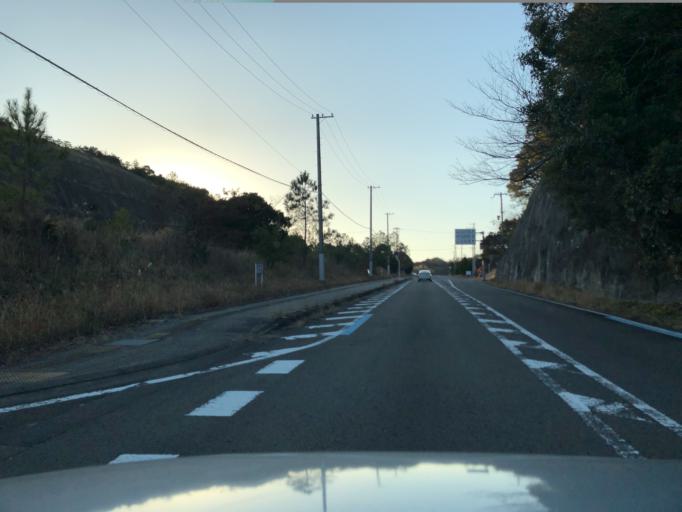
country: JP
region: Wakayama
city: Tanabe
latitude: 33.6612
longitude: 135.3810
